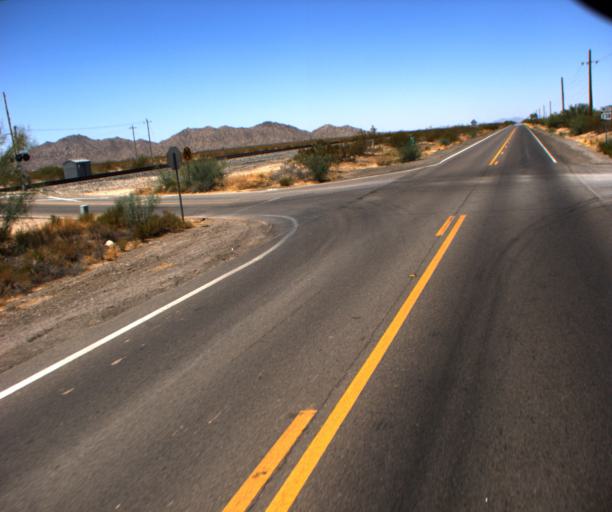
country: US
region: Arizona
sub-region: Pinal County
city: Maricopa
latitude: 33.0776
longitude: -112.1505
